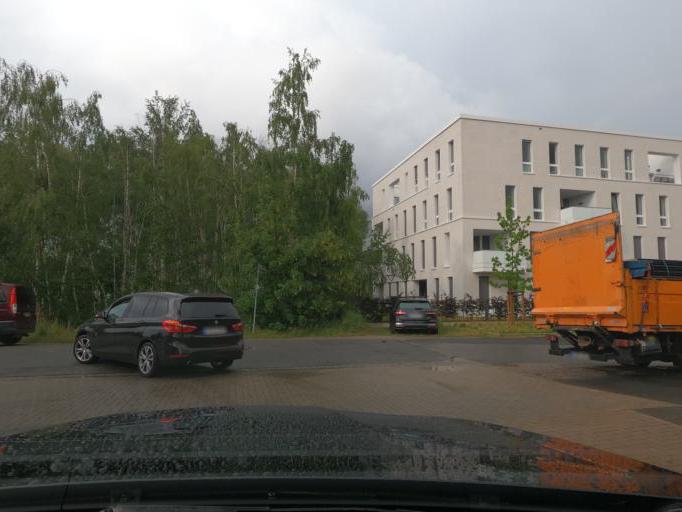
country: DE
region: Lower Saxony
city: Isernhagen Farster Bauerschaft
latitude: 52.3925
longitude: 9.8354
